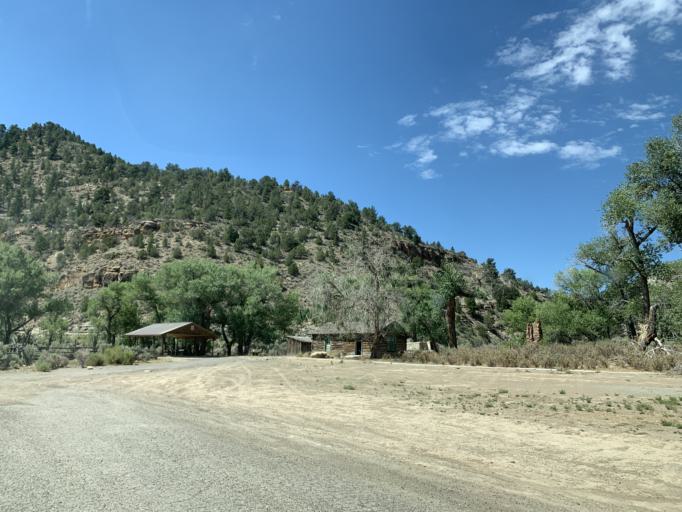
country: US
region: Utah
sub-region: Carbon County
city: East Carbon City
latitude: 39.7864
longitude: -110.4112
